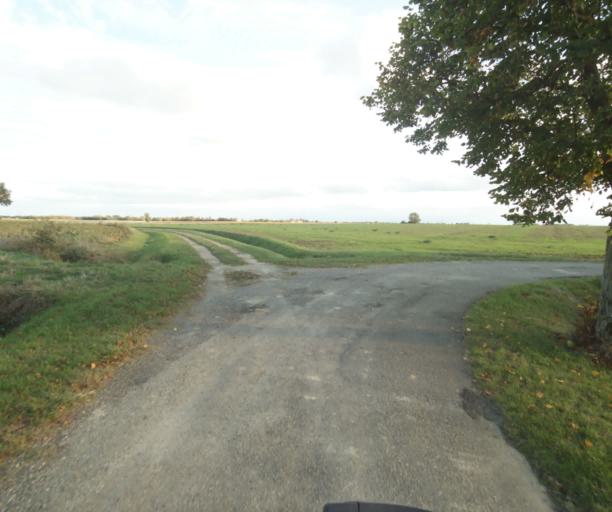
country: FR
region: Midi-Pyrenees
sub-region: Departement du Tarn-et-Garonne
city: Verdun-sur-Garonne
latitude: 43.8354
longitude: 1.1701
